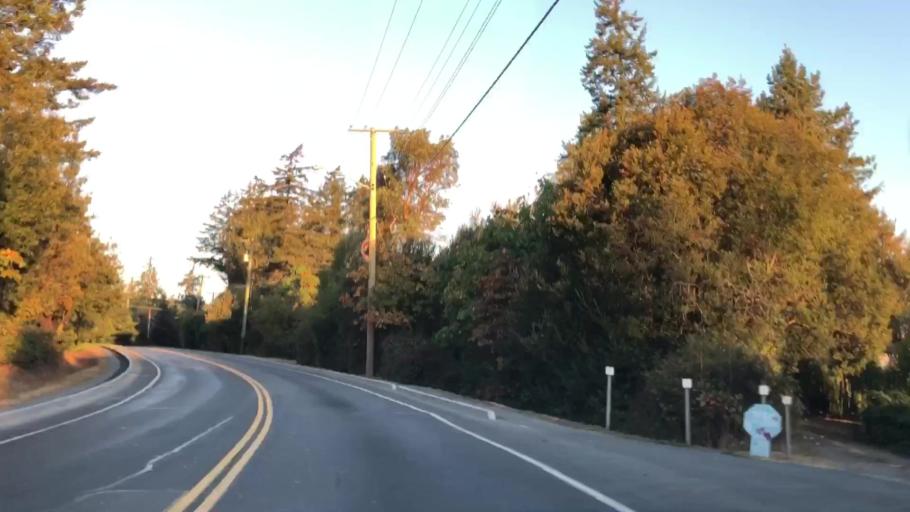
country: CA
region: British Columbia
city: Colwood
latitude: 48.4596
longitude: -123.4460
